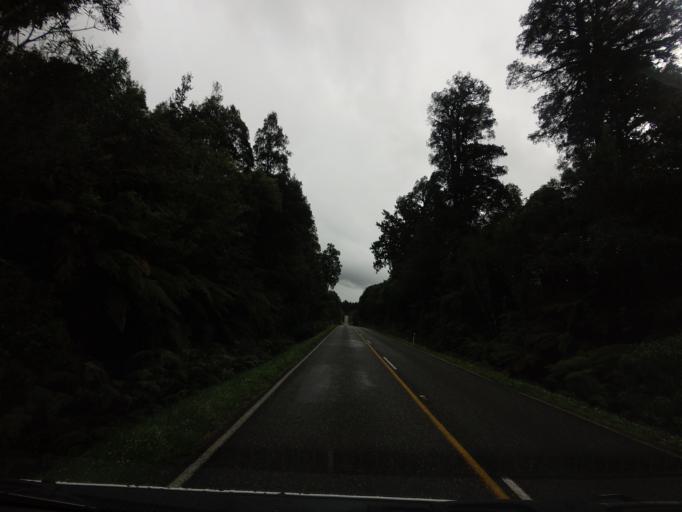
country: NZ
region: West Coast
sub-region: Westland District
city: Hokitika
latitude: -43.0300
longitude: 170.6584
